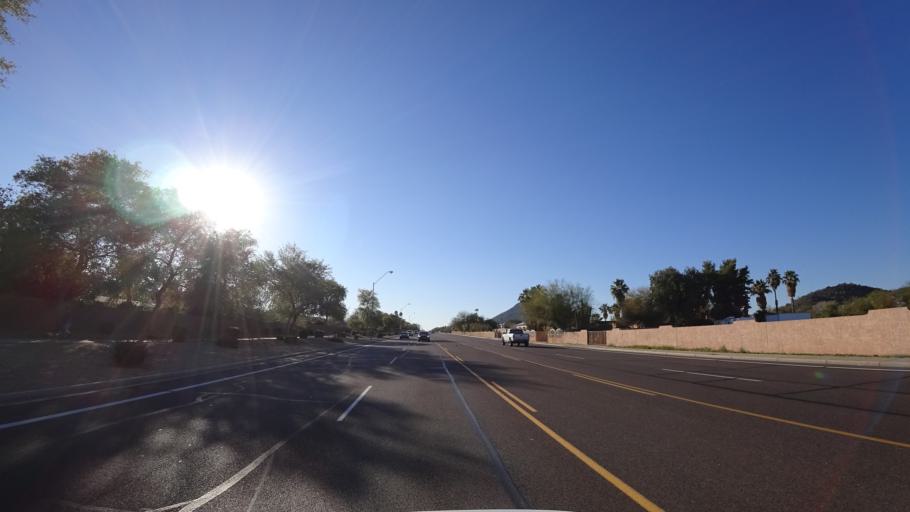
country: US
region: Arizona
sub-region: Maricopa County
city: Peoria
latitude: 33.7126
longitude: -112.1579
